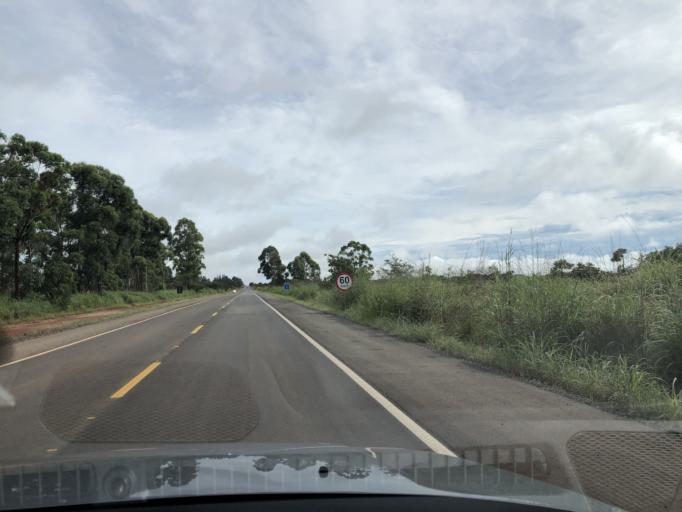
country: BR
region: Federal District
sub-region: Brasilia
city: Brasilia
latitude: -15.6582
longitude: -48.0841
